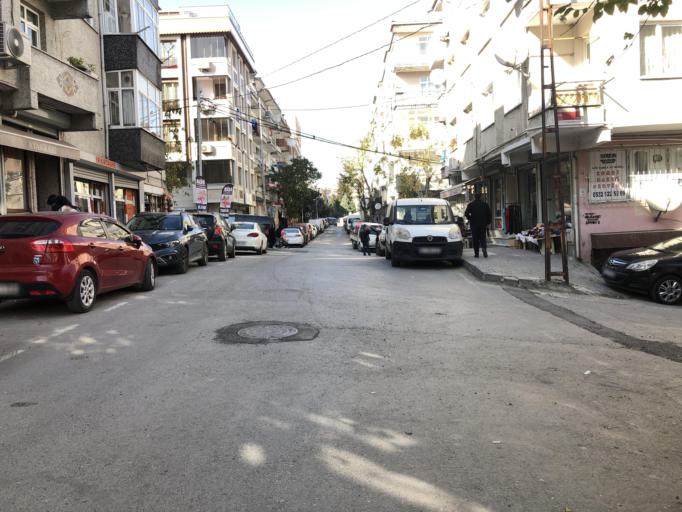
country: TR
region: Istanbul
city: Esenler
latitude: 41.0704
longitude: 28.9016
